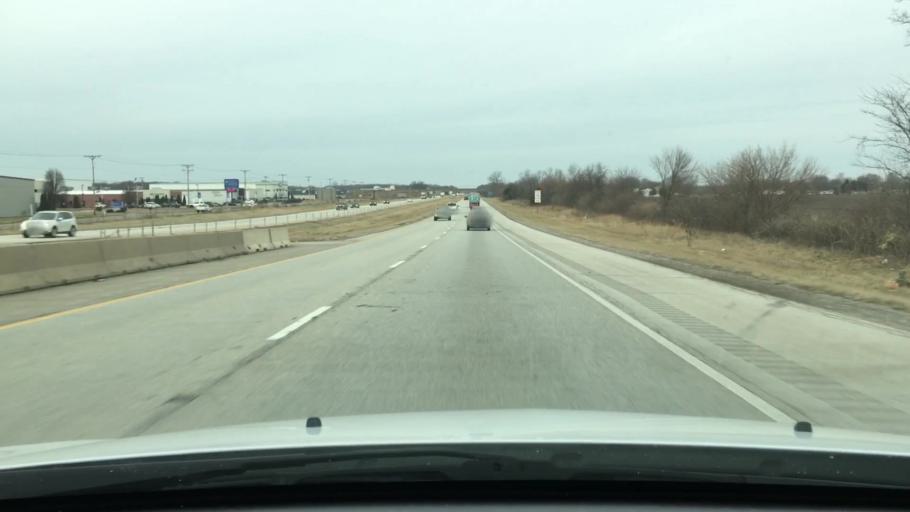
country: US
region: Illinois
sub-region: Sangamon County
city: Grandview
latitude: 39.8385
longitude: -89.5936
